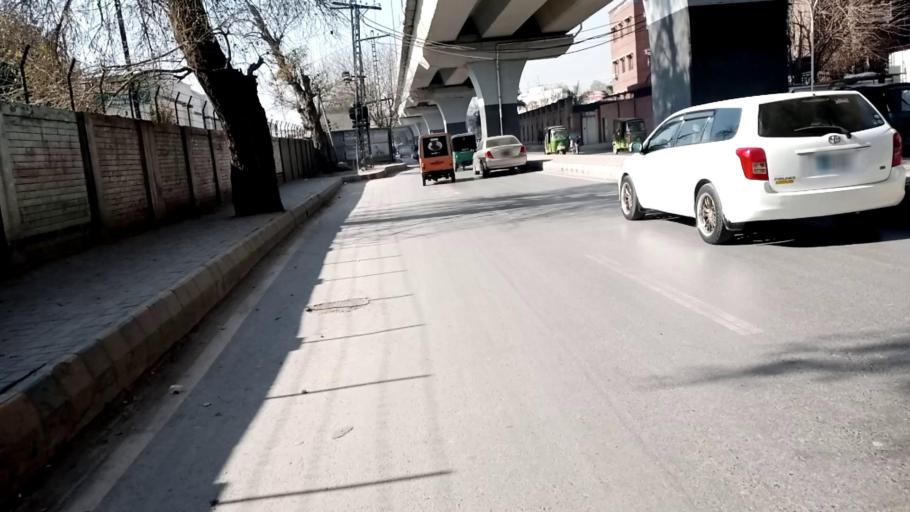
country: PK
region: Khyber Pakhtunkhwa
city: Peshawar
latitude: 34.0039
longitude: 71.5518
